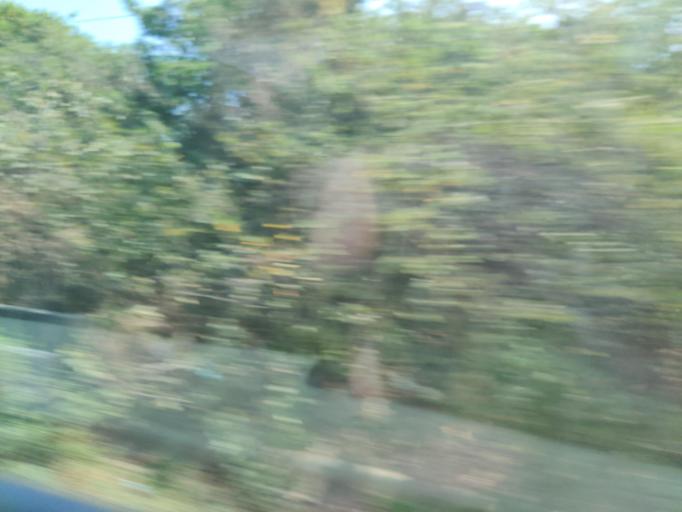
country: CO
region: Bolivar
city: Santa Catalina
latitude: 10.7469
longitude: -75.2638
